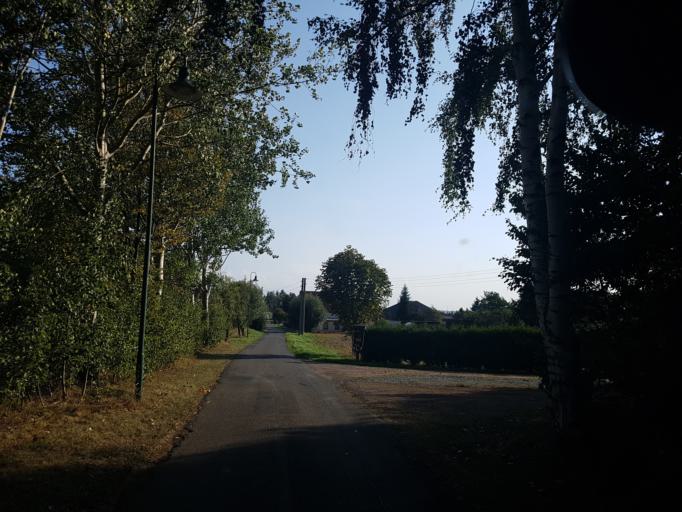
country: DE
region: Saxony
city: Dobeln
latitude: 51.1079
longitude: 13.0907
